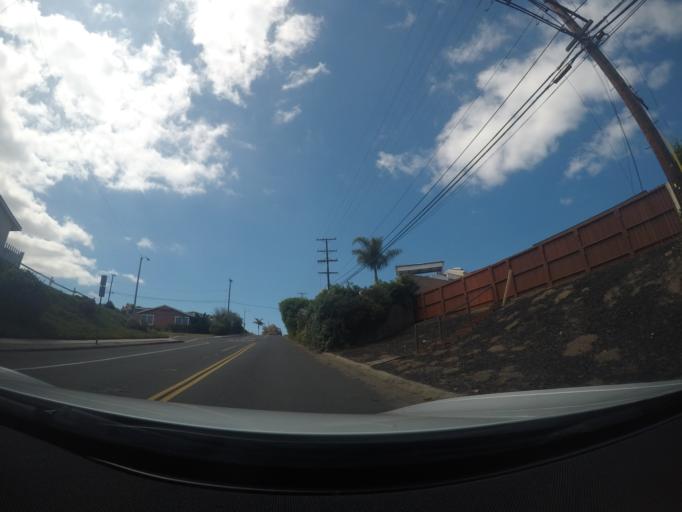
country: US
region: California
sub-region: Los Angeles County
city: Palos Verdes Estates
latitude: 33.8076
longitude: -118.3744
